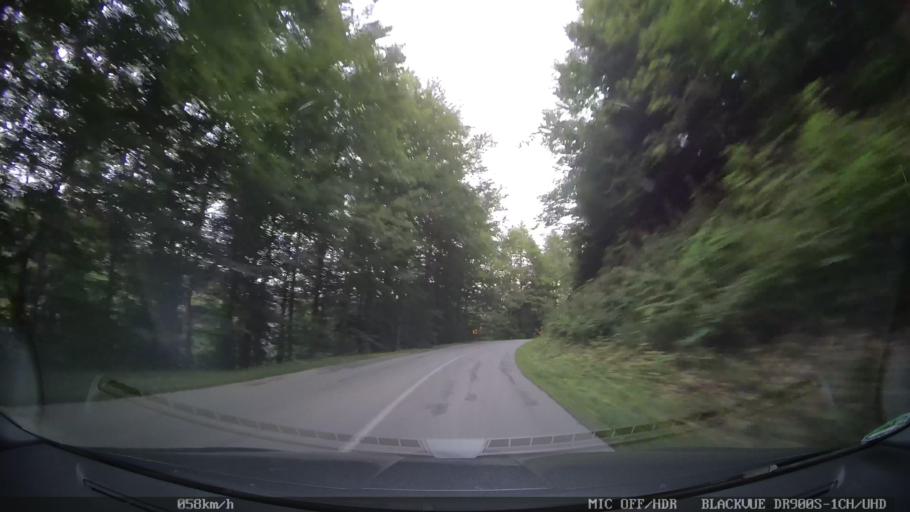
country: HR
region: Primorsko-Goranska
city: Vrbovsko
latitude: 45.2040
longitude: 15.0275
